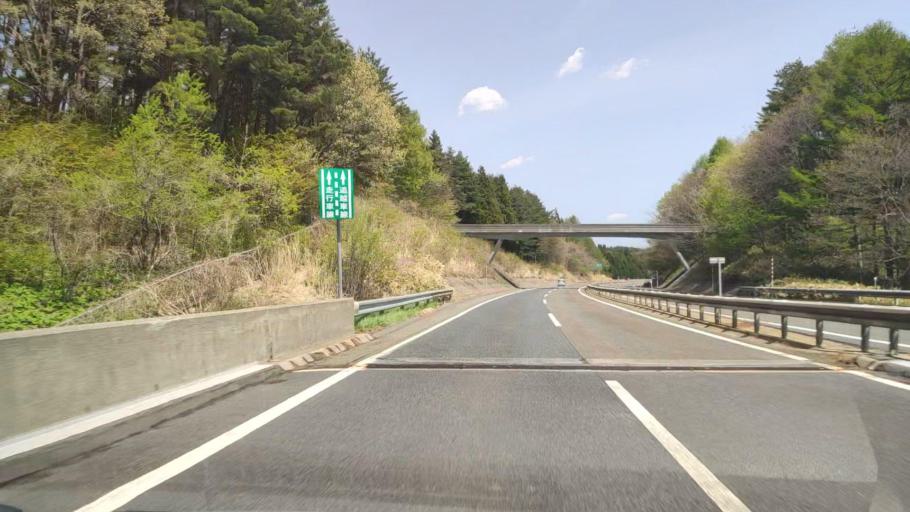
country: JP
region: Iwate
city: Ichinohe
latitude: 40.2740
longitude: 141.3996
